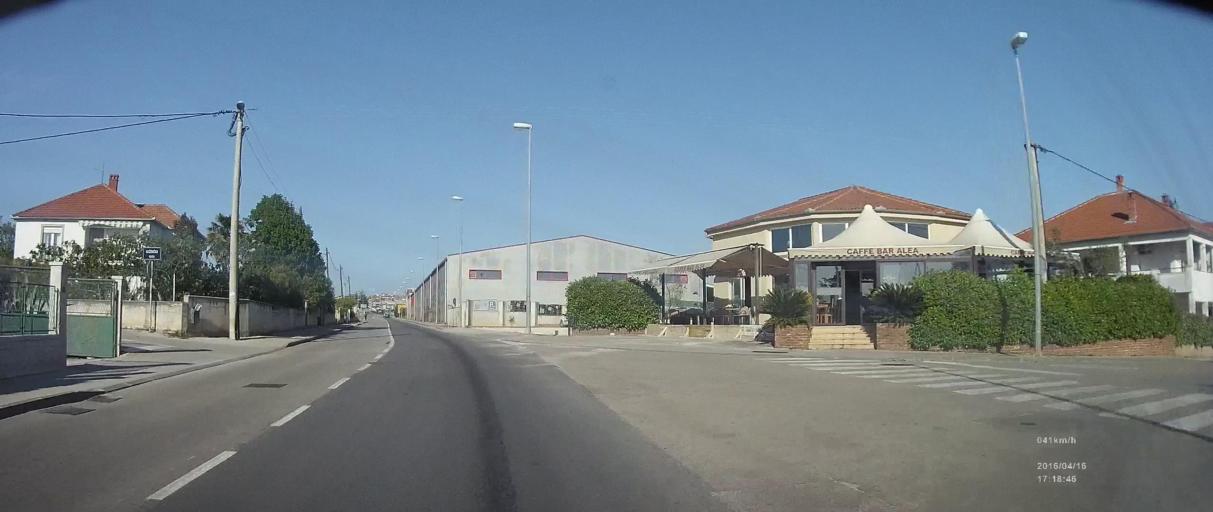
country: HR
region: Zadarska
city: Zadar
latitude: 44.1017
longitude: 15.2585
